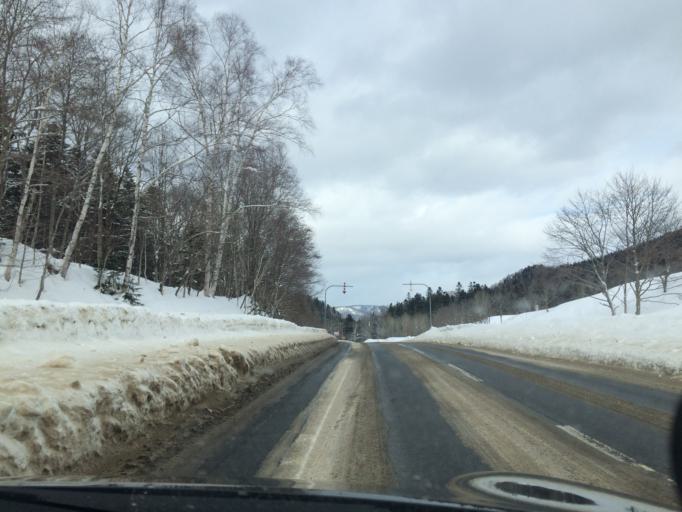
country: JP
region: Hokkaido
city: Shimo-furano
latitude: 42.9233
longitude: 142.3746
